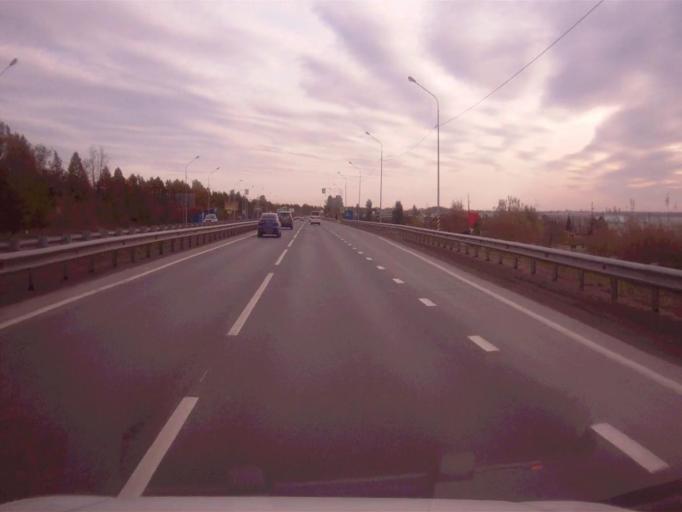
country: RU
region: Chelyabinsk
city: Novosineglazovskiy
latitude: 55.0324
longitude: 61.4446
